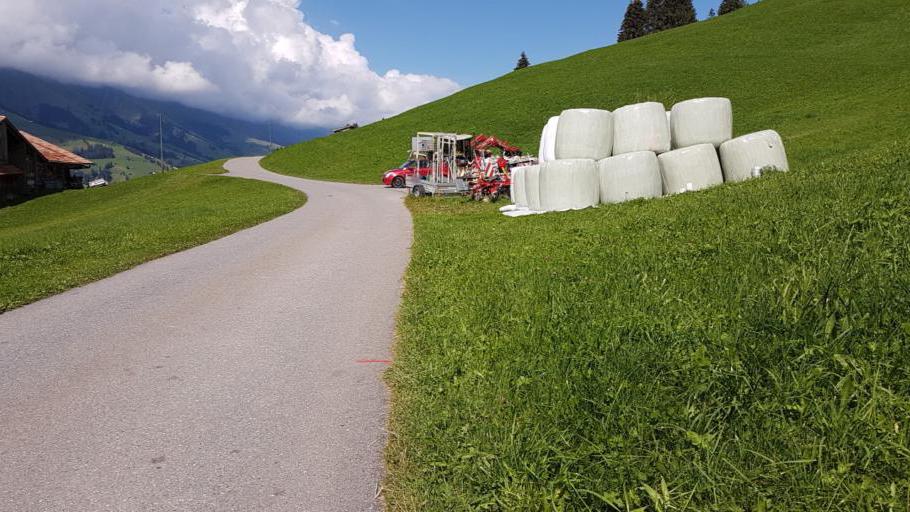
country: CH
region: Bern
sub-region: Frutigen-Niedersimmental District
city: Adelboden
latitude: 46.5040
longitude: 7.5899
